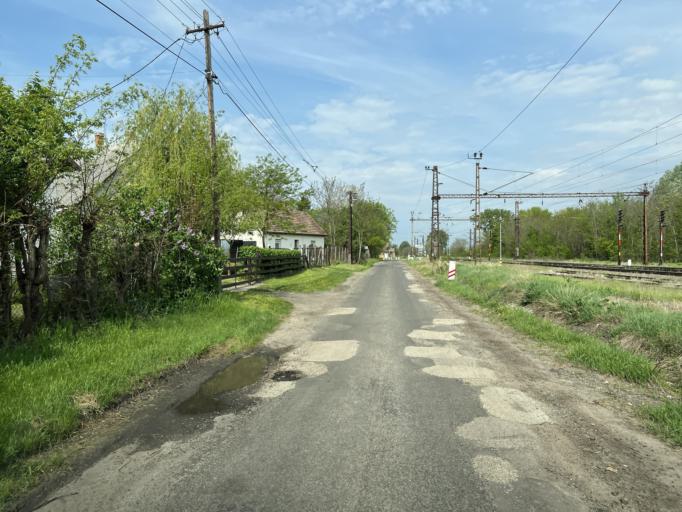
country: HU
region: Pest
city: Tapioszele
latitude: 47.3480
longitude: 19.8660
